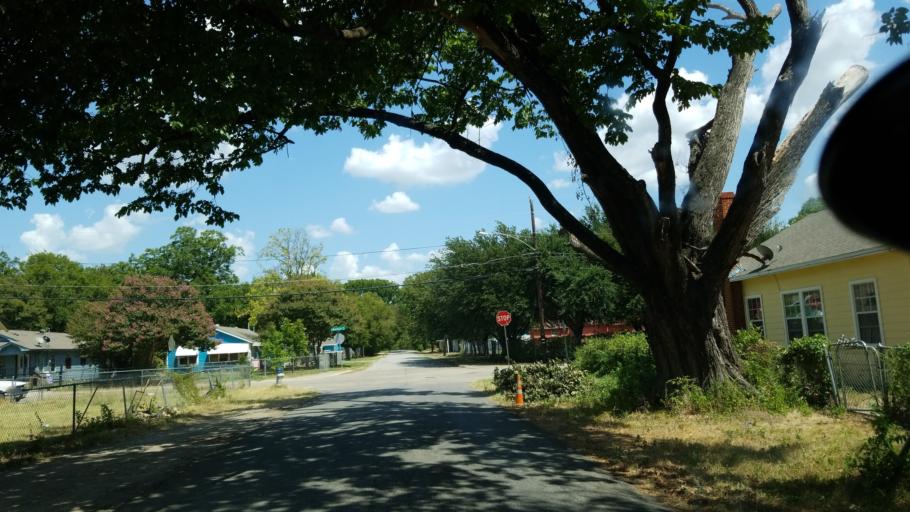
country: US
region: Texas
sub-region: Dallas County
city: Cockrell Hill
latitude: 32.7511
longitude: -96.9106
